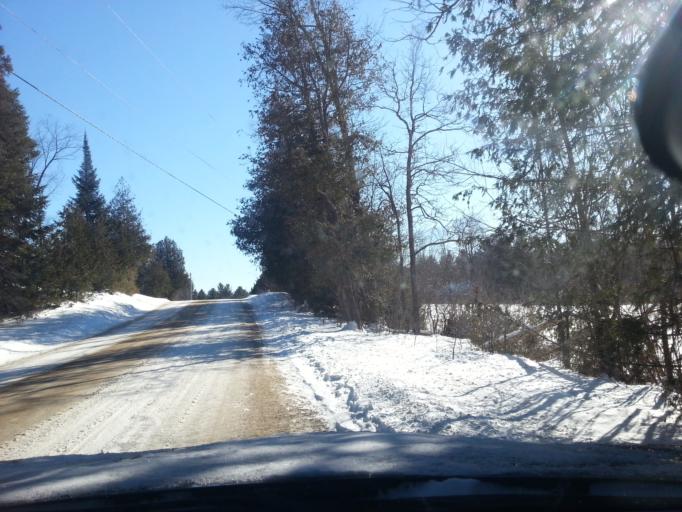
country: CA
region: Ontario
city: Arnprior
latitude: 45.2618
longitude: -76.3262
